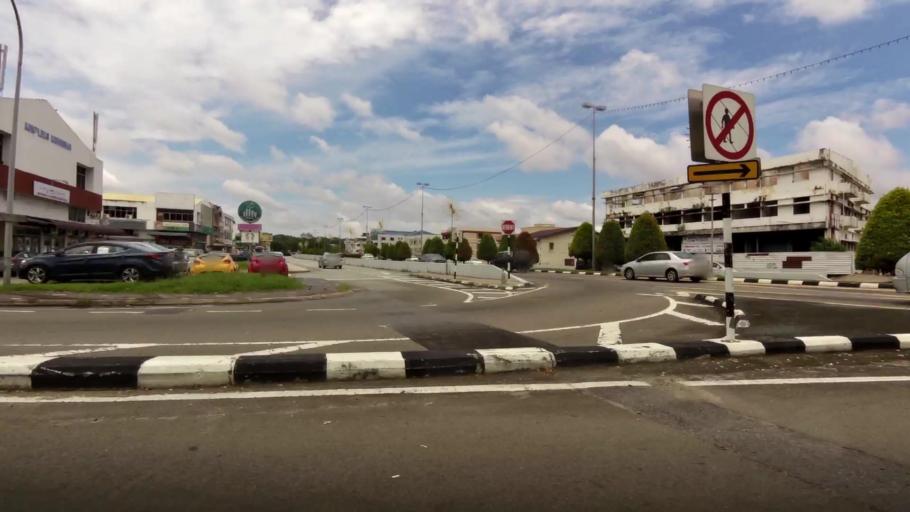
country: BN
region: Brunei and Muara
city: Bandar Seri Begawan
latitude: 4.9097
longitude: 114.9230
